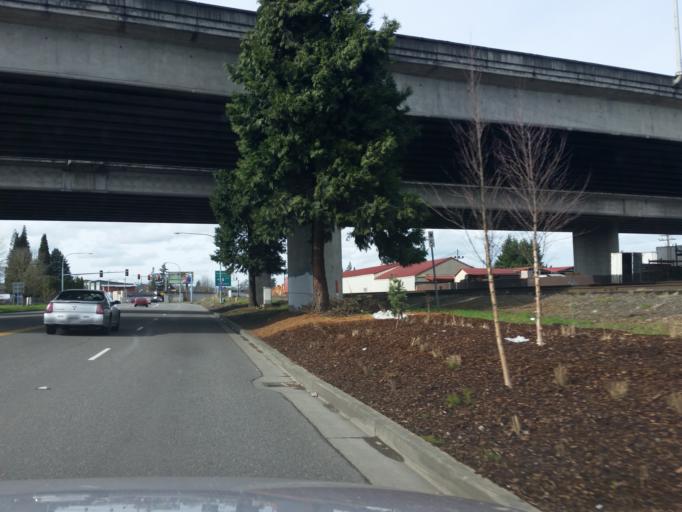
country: US
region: Washington
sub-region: Pierce County
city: Puyallup
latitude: 47.1901
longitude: -122.2820
